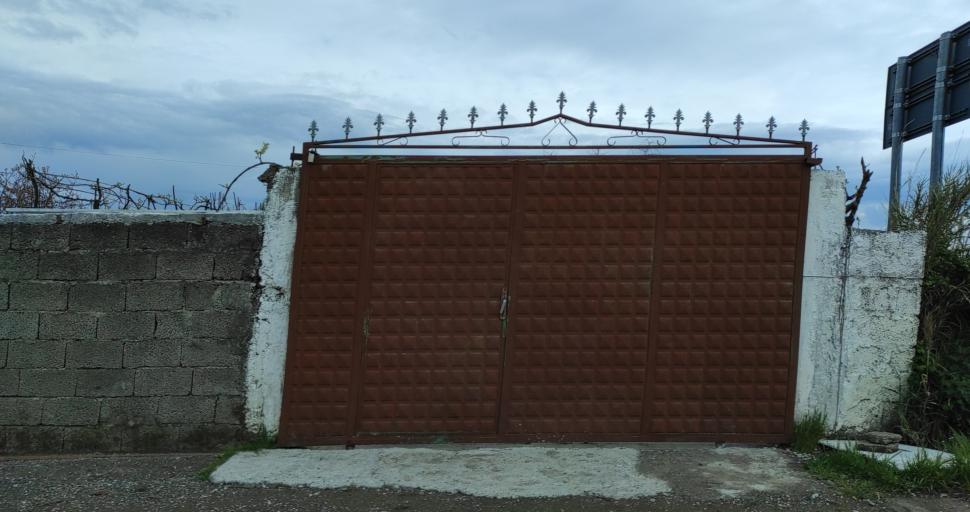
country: AL
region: Shkoder
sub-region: Rrethi i Shkodres
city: Berdica e Madhe
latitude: 42.0267
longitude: 19.4696
